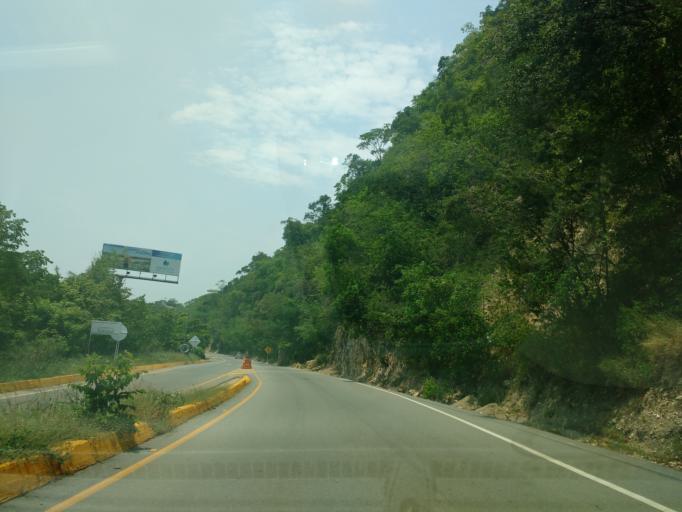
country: CO
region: Cundinamarca
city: Ricaurte
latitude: 4.2465
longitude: -74.7440
